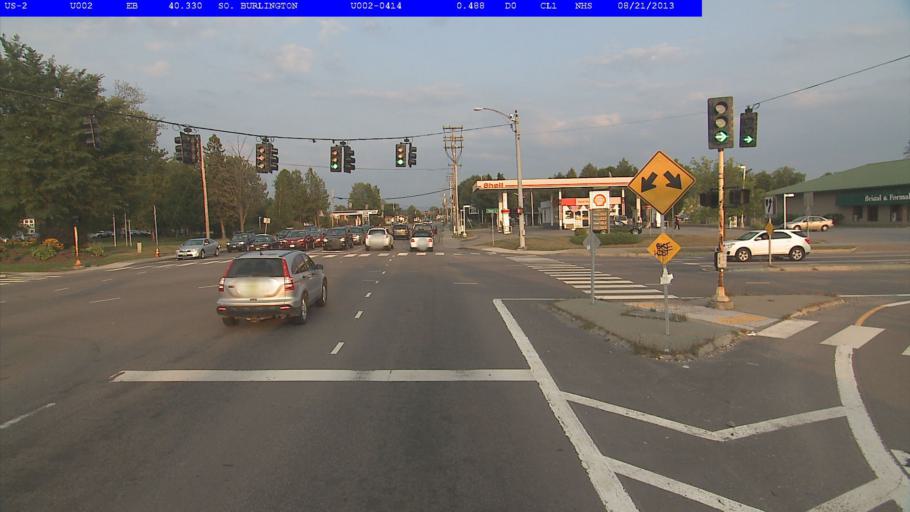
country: US
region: Vermont
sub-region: Chittenden County
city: South Burlington
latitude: 44.4692
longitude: -73.1815
